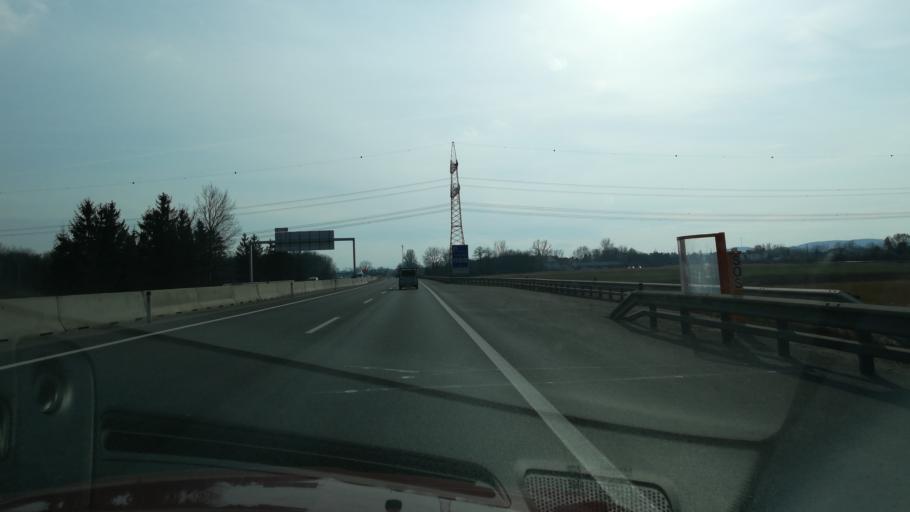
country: AT
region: Lower Austria
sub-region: Politischer Bezirk Sankt Polten
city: Traismauer
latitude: 48.3302
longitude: 15.7208
